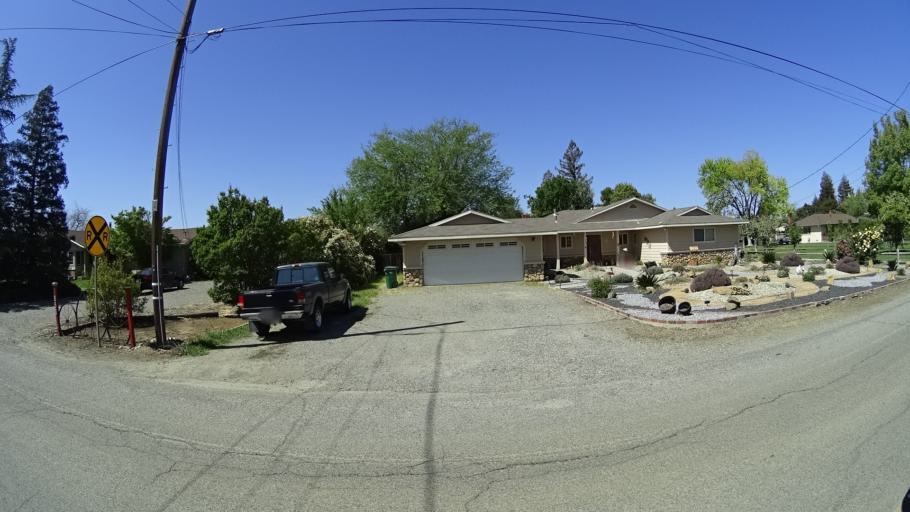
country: US
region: California
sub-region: Glenn County
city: Willows
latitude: 39.5325
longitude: -122.2074
